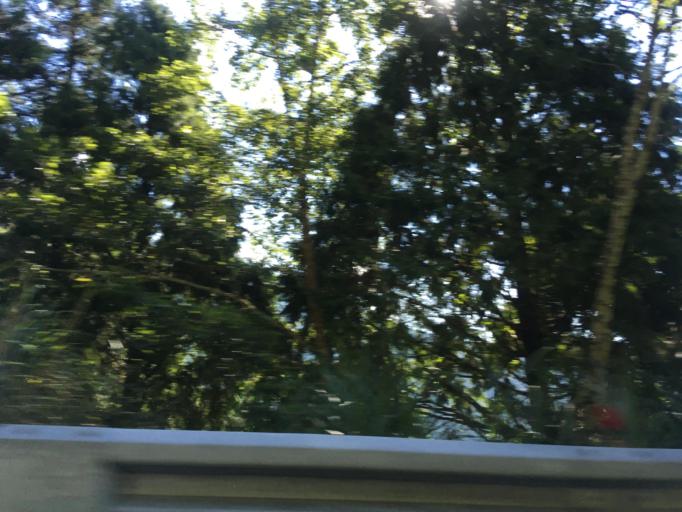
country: TW
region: Taiwan
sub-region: Yilan
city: Yilan
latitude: 24.4996
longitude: 121.5536
